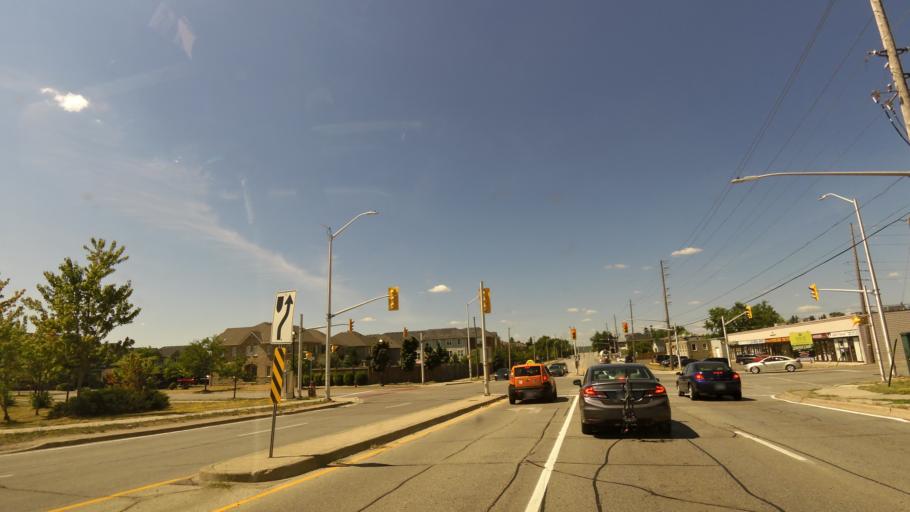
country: CA
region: Ontario
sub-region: Halton
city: Milton
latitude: 43.6534
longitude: -79.9077
